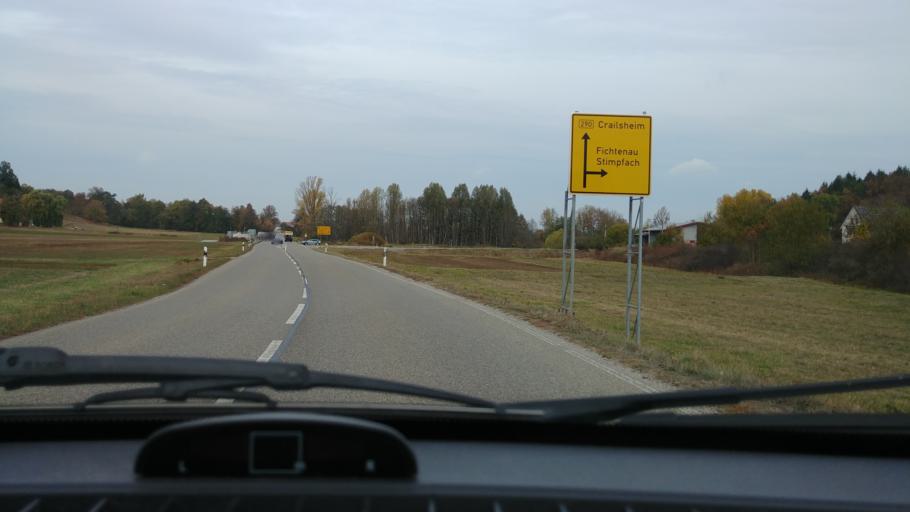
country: DE
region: Baden-Wuerttemberg
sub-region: Regierungsbezirk Stuttgart
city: Stimpfach
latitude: 49.0587
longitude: 10.0816
